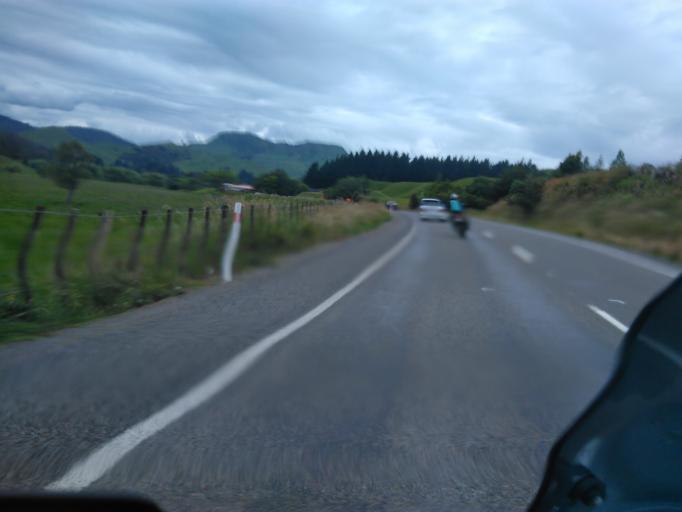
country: NZ
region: Bay of Plenty
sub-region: Opotiki District
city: Opotiki
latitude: -38.3642
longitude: 177.5170
